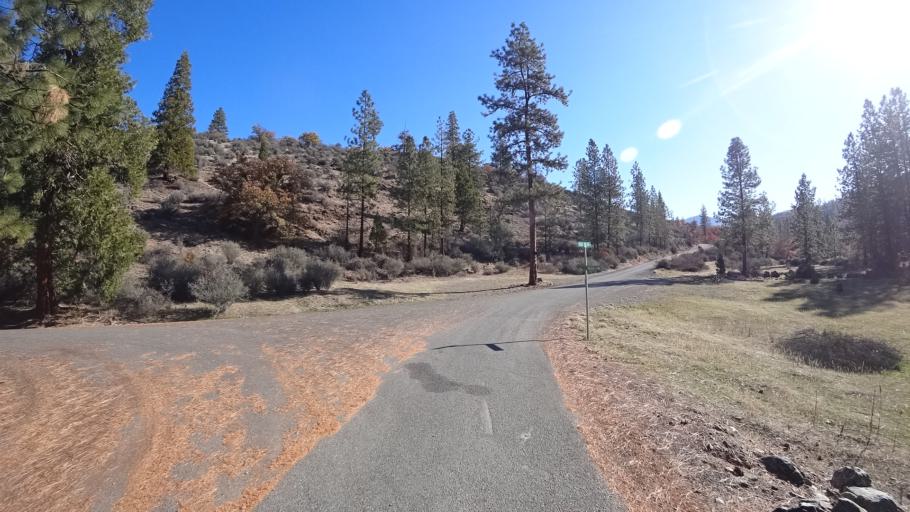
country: US
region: California
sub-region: Siskiyou County
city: Yreka
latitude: 41.8346
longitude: -122.8386
